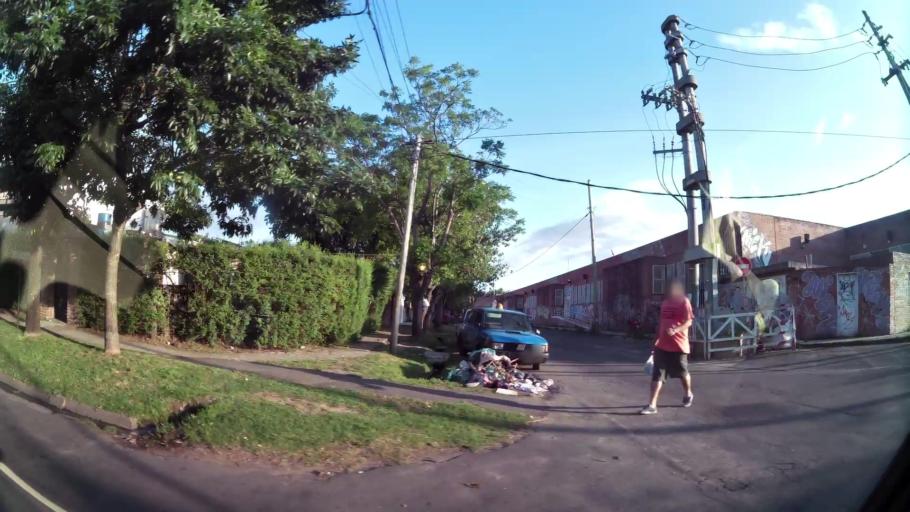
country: AR
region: Buenos Aires
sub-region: Partido de Tigre
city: Tigre
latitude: -34.4561
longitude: -58.6379
